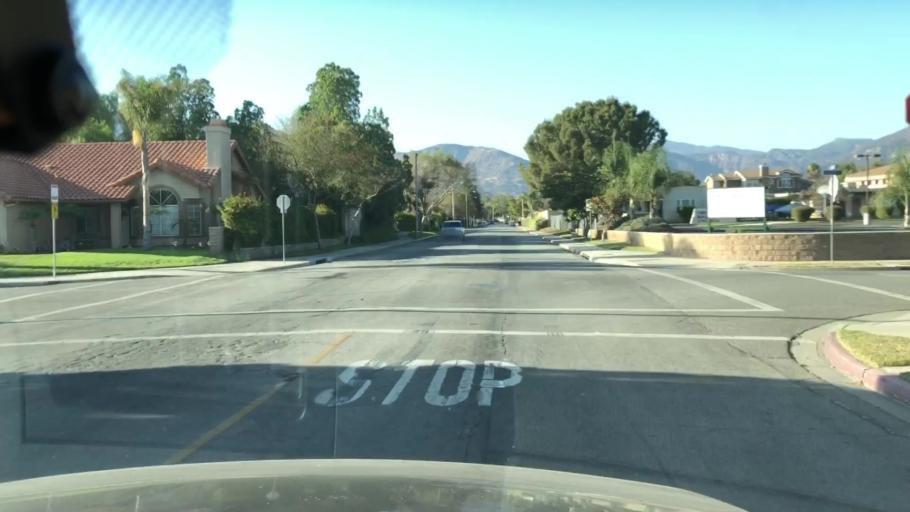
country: US
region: California
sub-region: Ventura County
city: Fillmore
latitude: 34.4005
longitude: -118.9283
